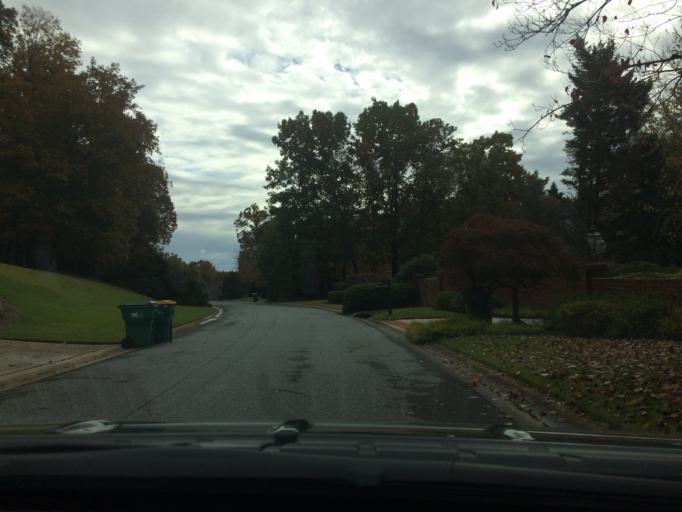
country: US
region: Georgia
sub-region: Fulton County
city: Johns Creek
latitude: 34.0082
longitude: -84.2453
